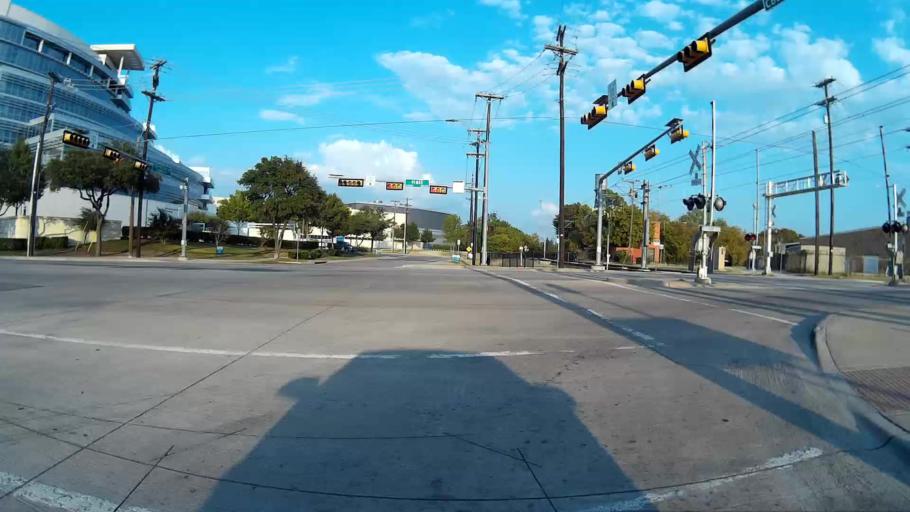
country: US
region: Texas
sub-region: Dallas County
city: Dallas
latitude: 32.7870
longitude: -96.7797
